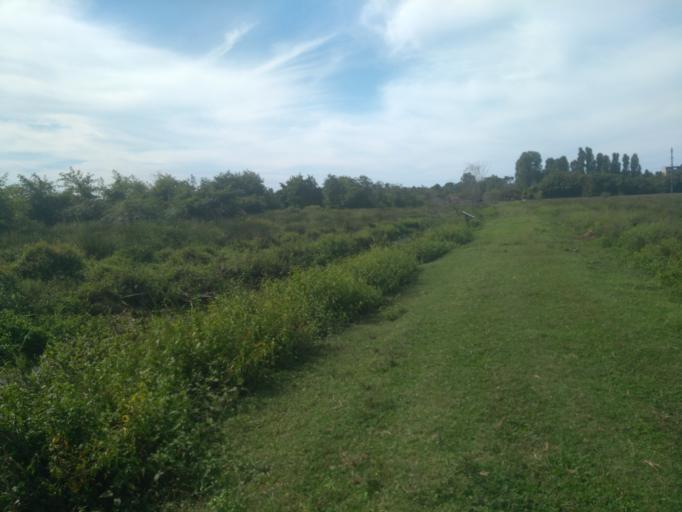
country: GE
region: Ajaria
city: Kobuleti
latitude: 41.8634
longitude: 41.7881
